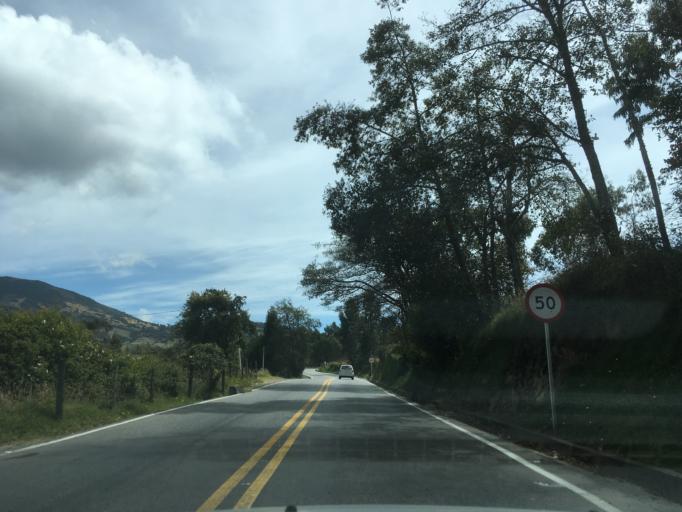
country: CO
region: Boyaca
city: Firavitoba
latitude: 5.6242
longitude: -72.9178
